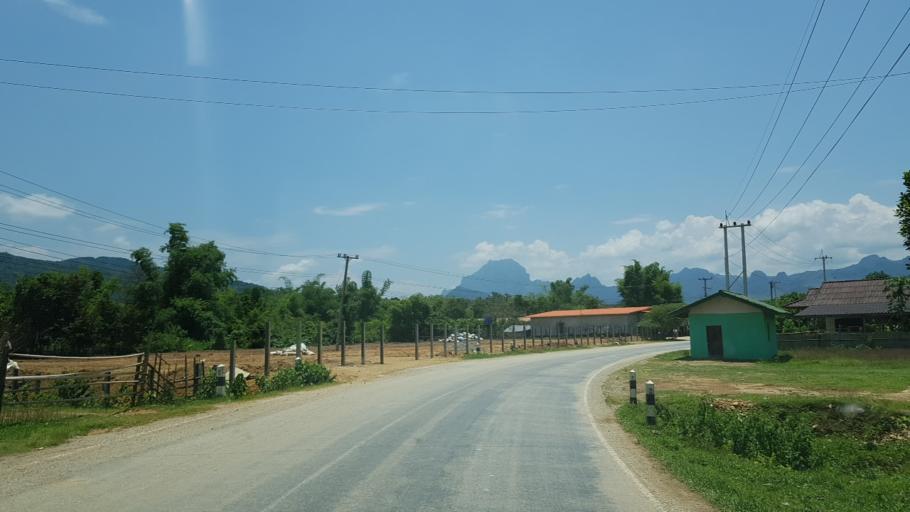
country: LA
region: Vientiane
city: Muang Kasi
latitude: 19.2527
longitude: 102.2412
